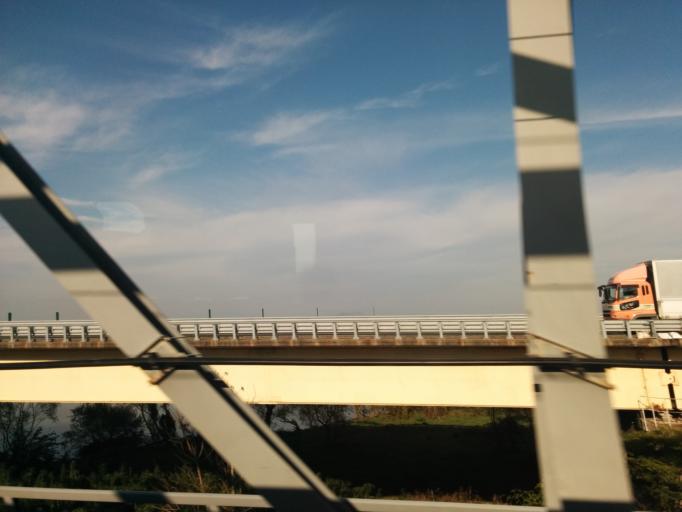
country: JP
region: Aichi
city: Sobue
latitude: 35.2940
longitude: 136.7275
